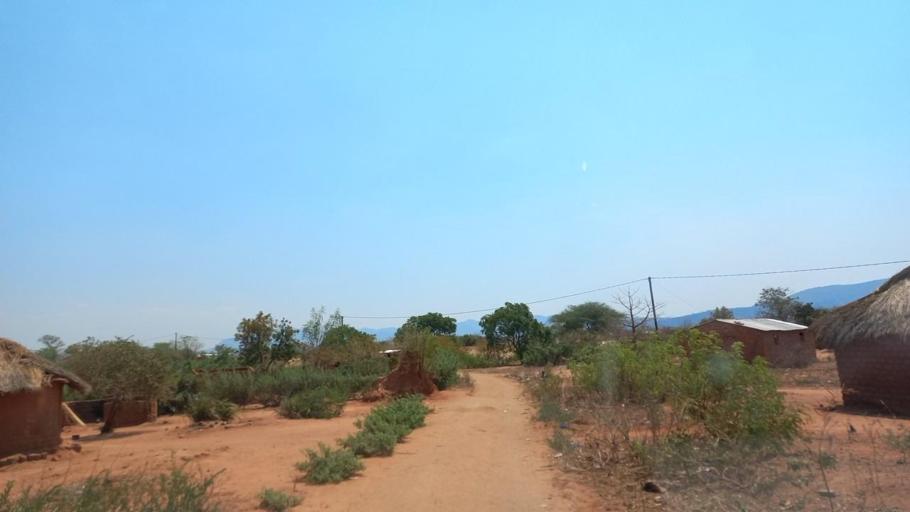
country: ZM
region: Lusaka
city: Luangwa
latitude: -15.6045
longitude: 30.4016
